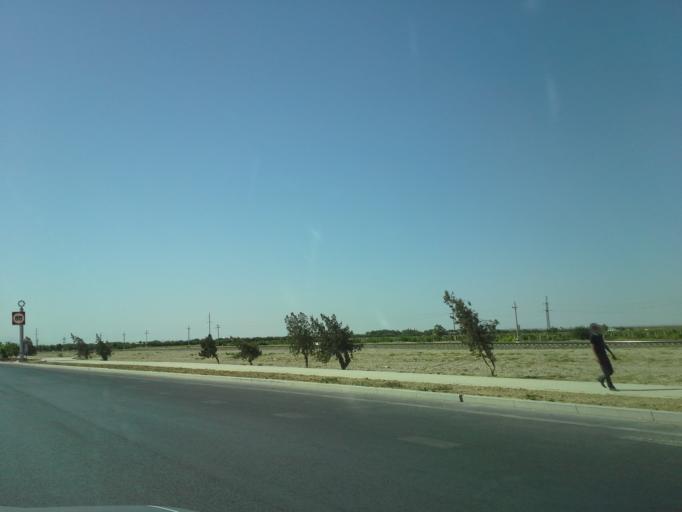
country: TM
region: Ahal
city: Annau
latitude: 37.9147
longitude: 58.4791
